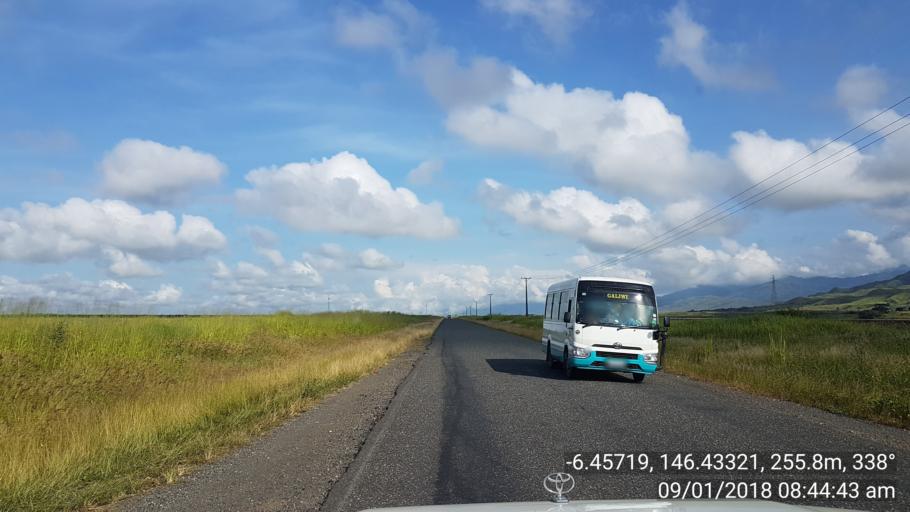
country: PG
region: Eastern Highlands
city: Kainantu
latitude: -6.4572
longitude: 146.4335
